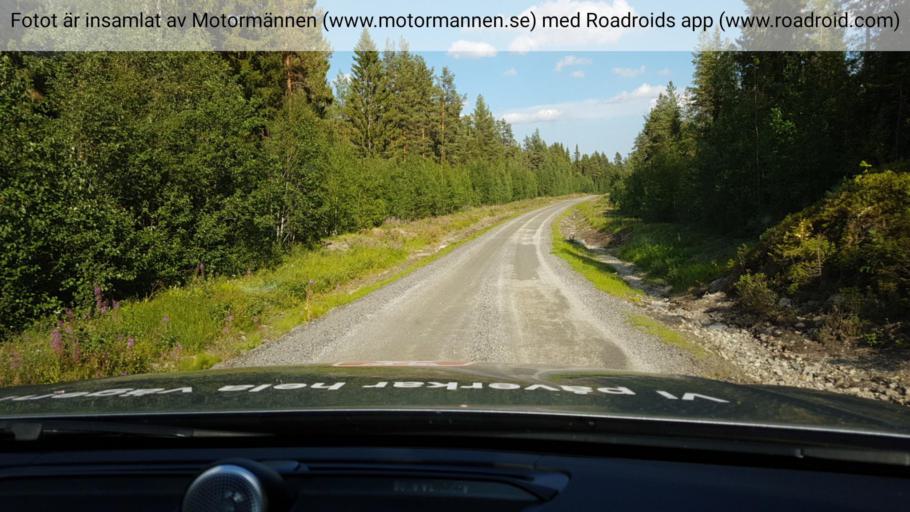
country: SE
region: Vaesterbotten
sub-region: Dorotea Kommun
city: Dorotea
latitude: 63.9215
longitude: 16.2345
